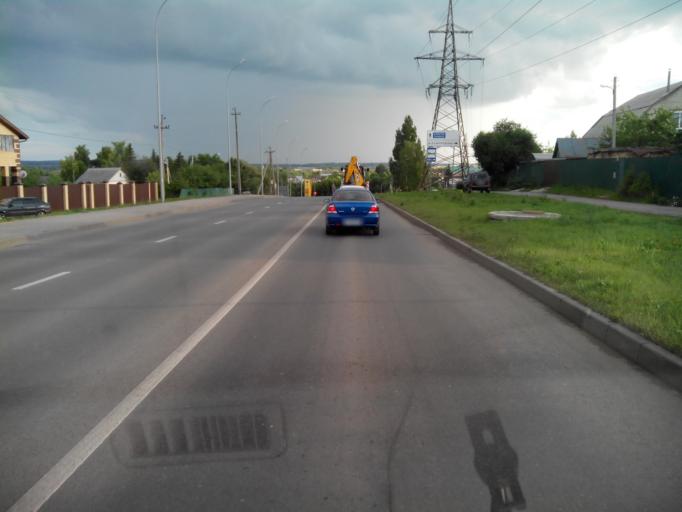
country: RU
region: Penza
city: Penza
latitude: 53.1555
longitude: 44.9770
